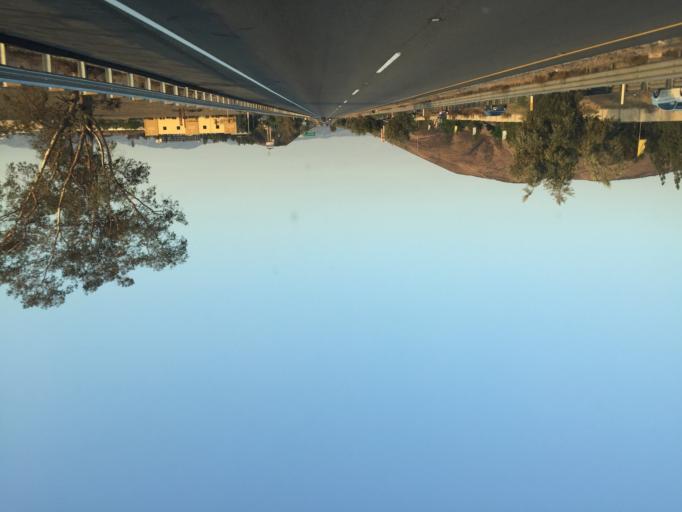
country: US
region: California
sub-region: San Bernardino County
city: Muscoy
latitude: 34.1698
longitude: -117.3381
